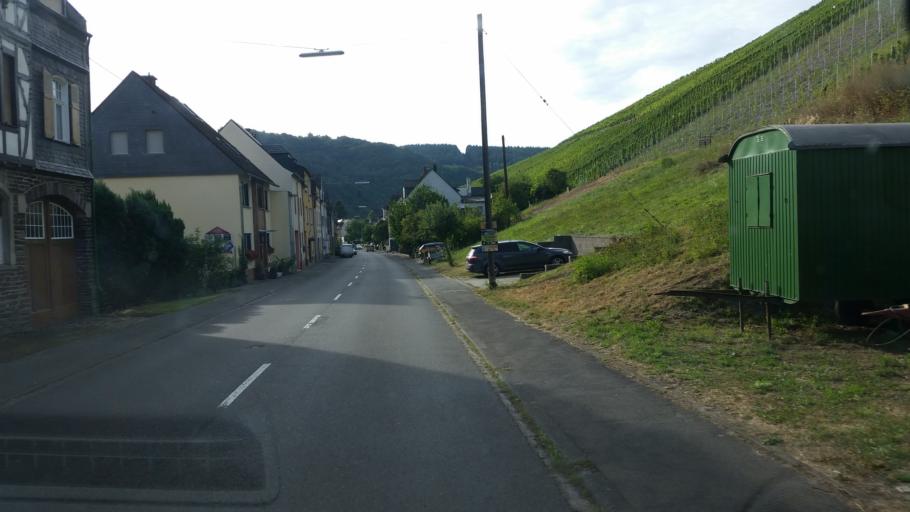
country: DE
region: Rheinland-Pfalz
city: Enkirch
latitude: 49.9841
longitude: 7.1323
